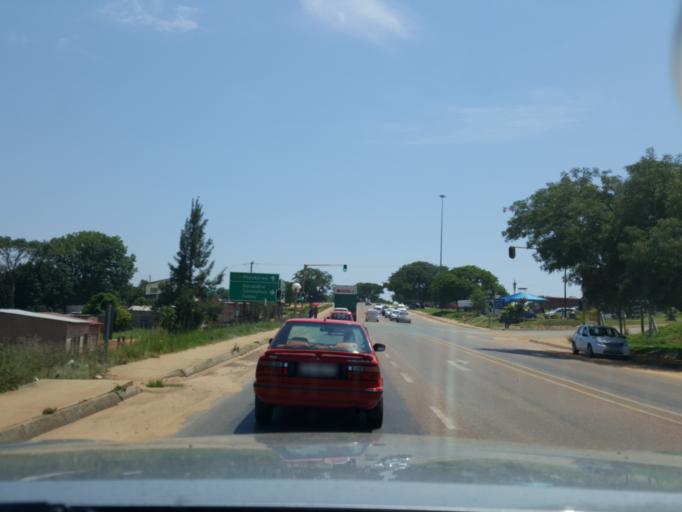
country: ZA
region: Limpopo
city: Thulamahashi
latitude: -24.9571
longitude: 31.1264
